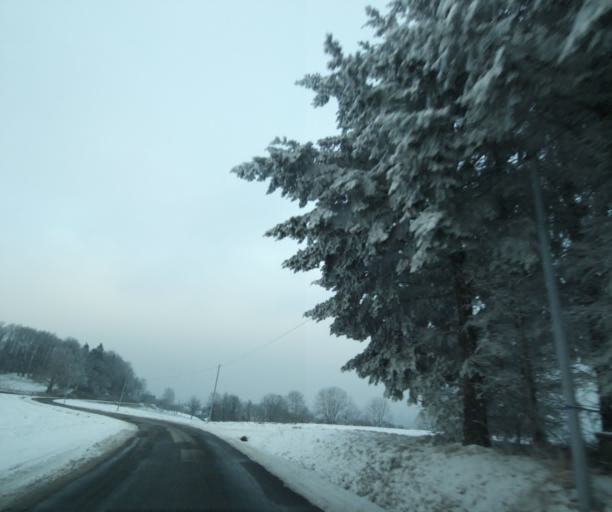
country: FR
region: Rhone-Alpes
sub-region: Departement de la Haute-Savoie
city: Reignier-Esery
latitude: 46.1204
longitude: 6.2361
